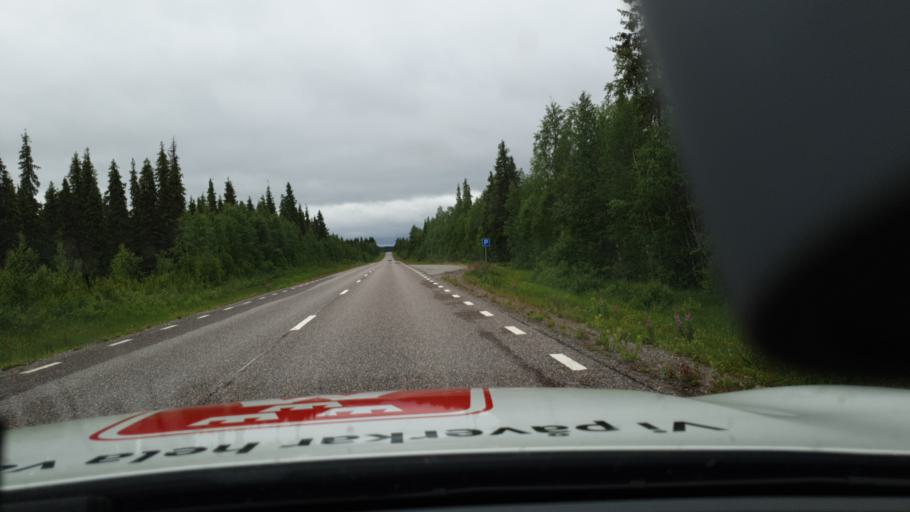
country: SE
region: Norrbotten
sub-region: Pajala Kommun
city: Pajala
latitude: 67.1406
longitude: 23.5745
